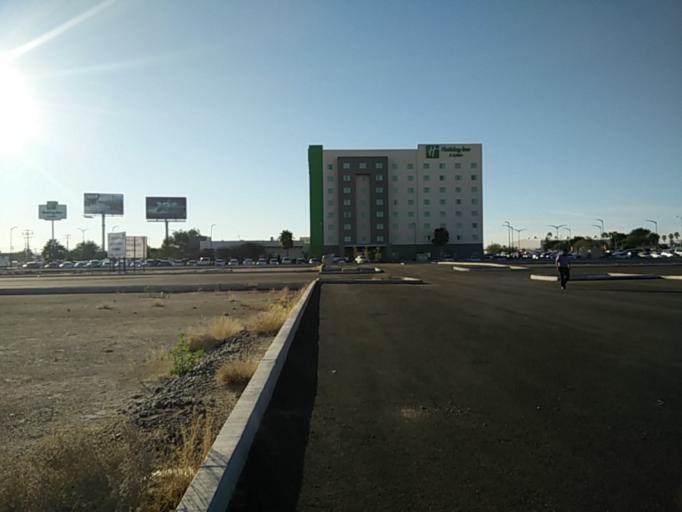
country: MX
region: Sonora
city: Hermosillo
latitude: 29.0962
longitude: -111.0240
